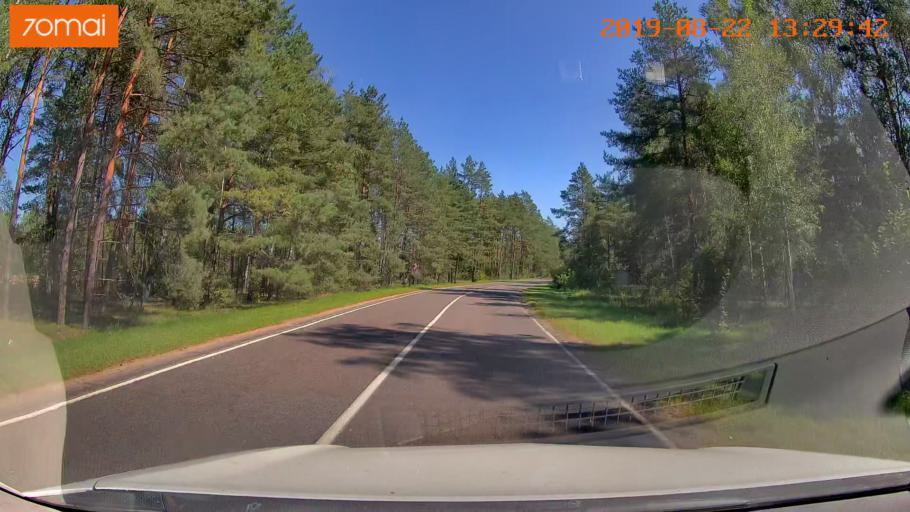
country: BY
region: Minsk
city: Staryya Darohi
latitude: 53.2172
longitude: 28.1383
